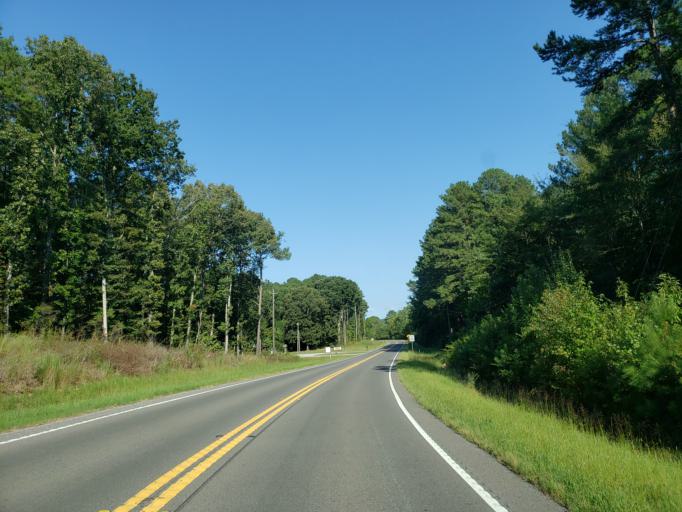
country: US
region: Georgia
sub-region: Whitfield County
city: Varnell
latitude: 34.9005
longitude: -85.0304
